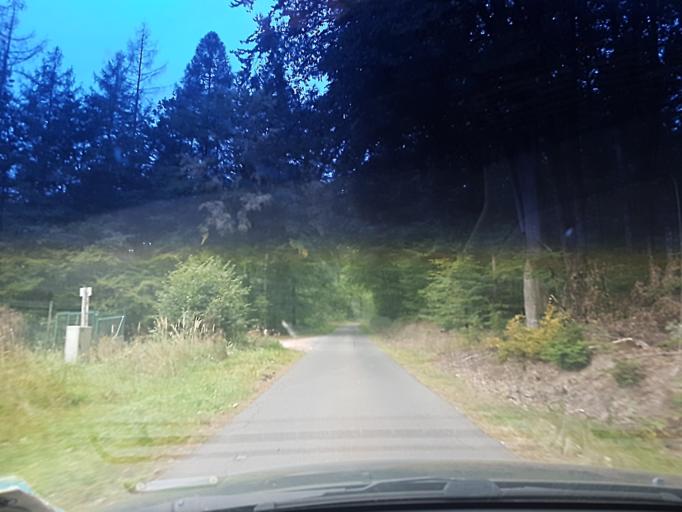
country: DE
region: Bavaria
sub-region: Regierungsbezirk Unterfranken
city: Geiselwind
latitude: 49.8171
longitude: 10.5049
